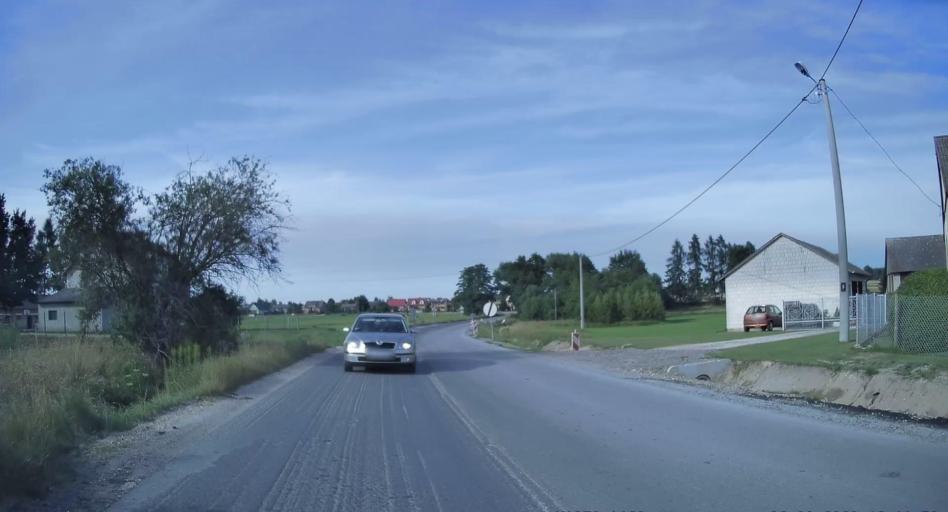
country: PL
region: Swietokrzyskie
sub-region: Powiat kielecki
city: Lopuszno
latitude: 50.9676
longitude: 20.2452
